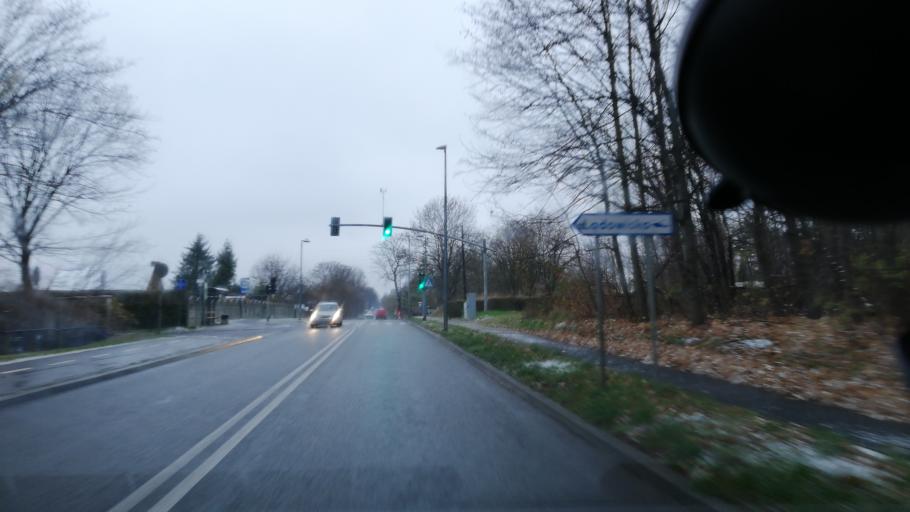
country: PL
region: Silesian Voivodeship
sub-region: Chorzow
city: Chorzow
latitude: 50.3010
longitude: 18.9816
